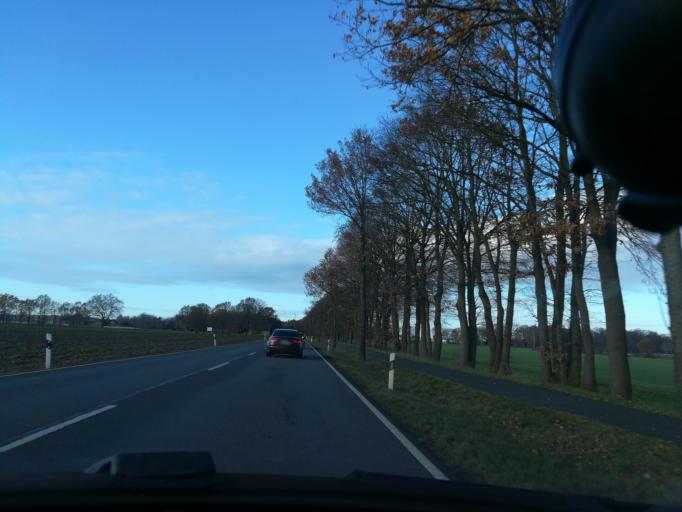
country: DE
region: Lower Saxony
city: Uchte
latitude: 52.4638
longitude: 8.9118
